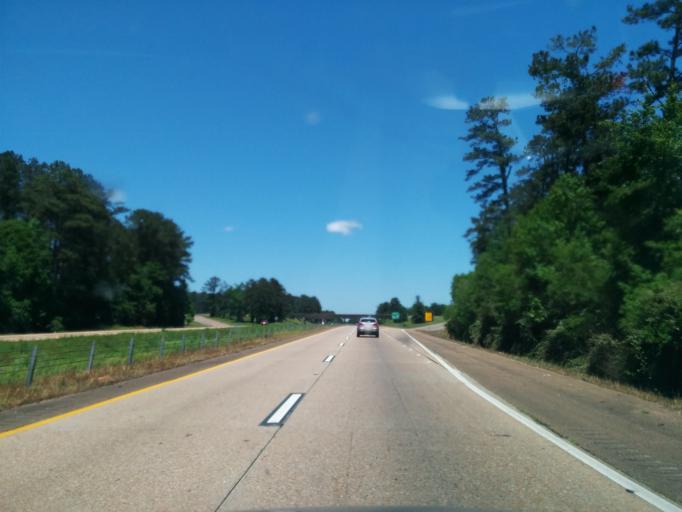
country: US
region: Mississippi
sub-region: Pike County
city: Magnolia
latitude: 31.1427
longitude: -90.4802
